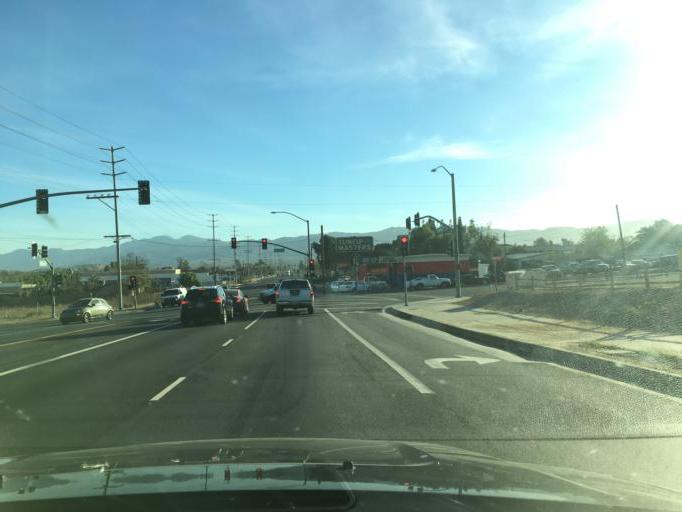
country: US
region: California
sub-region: Riverside County
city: Norco
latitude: 33.9317
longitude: -117.5578
